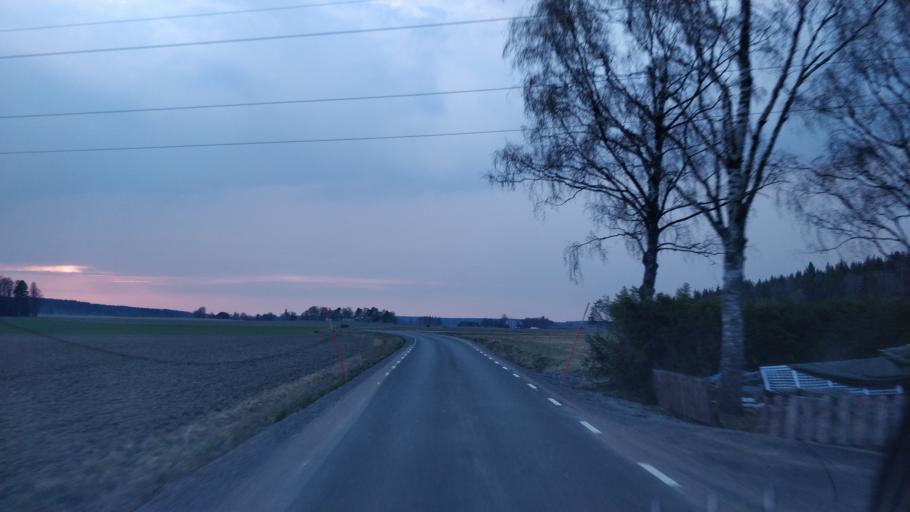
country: SE
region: Uppsala
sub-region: Enkopings Kommun
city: Orsundsbro
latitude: 59.7245
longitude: 17.2222
